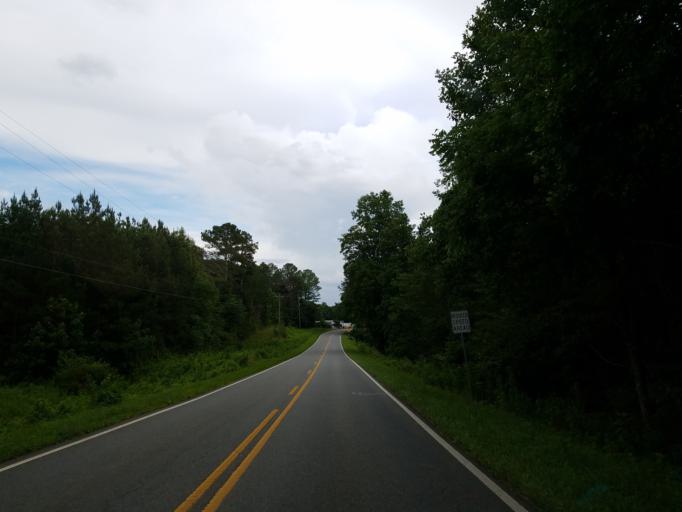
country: US
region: Georgia
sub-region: Gilmer County
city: Ellijay
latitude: 34.6763
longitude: -84.3712
